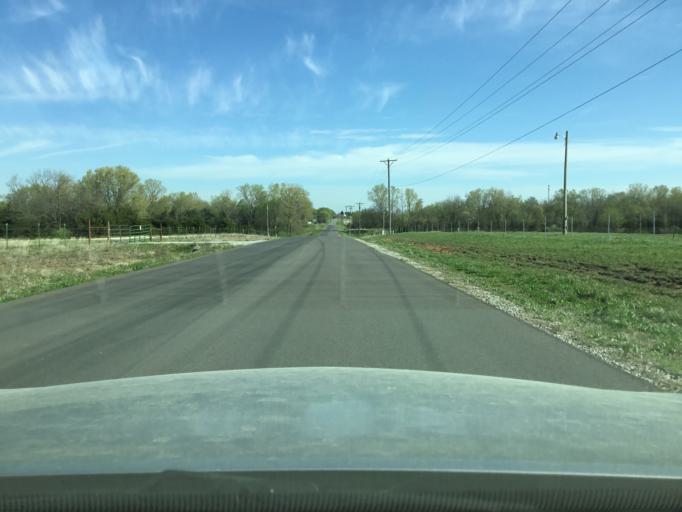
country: US
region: Kansas
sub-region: Neosho County
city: Chanute
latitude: 37.6549
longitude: -95.4435
